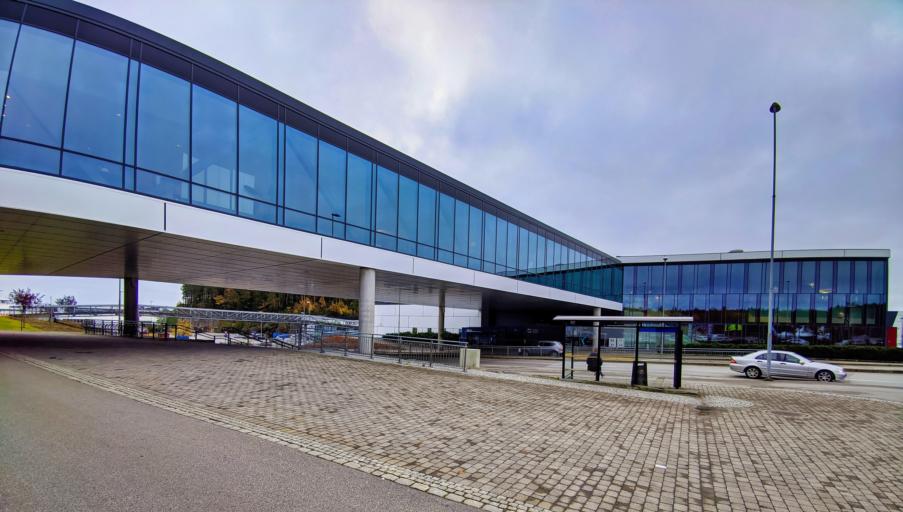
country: NO
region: Vest-Agder
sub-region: Kristiansand
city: Tveit
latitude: 58.1789
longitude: 8.1285
